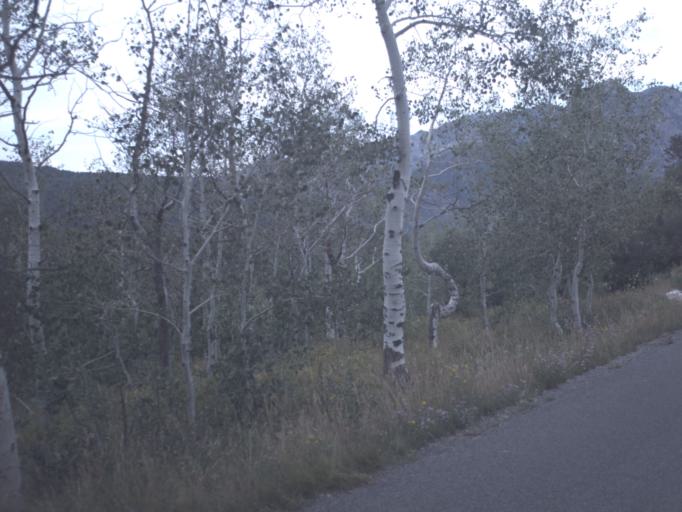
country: US
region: Utah
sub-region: Utah County
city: Lindon
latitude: 40.4350
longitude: -111.6157
